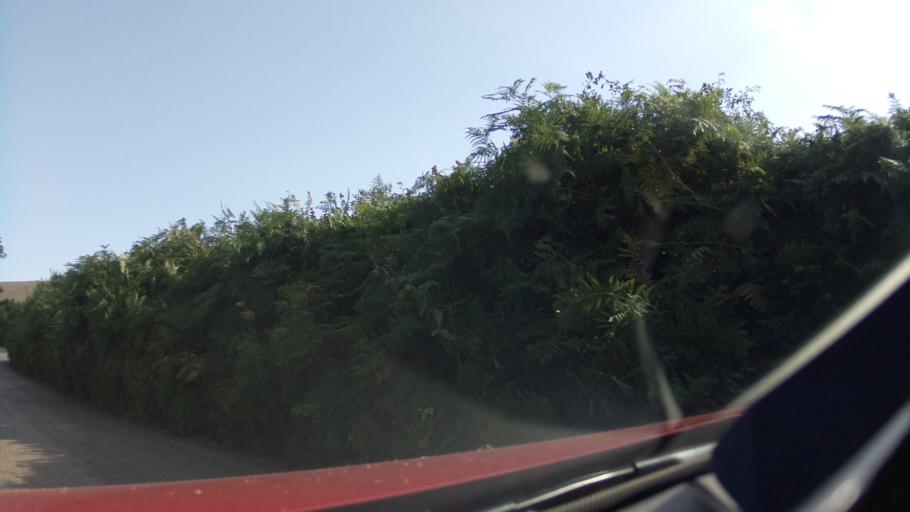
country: GB
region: England
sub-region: Devon
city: Totnes
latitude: 50.4271
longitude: -3.7434
